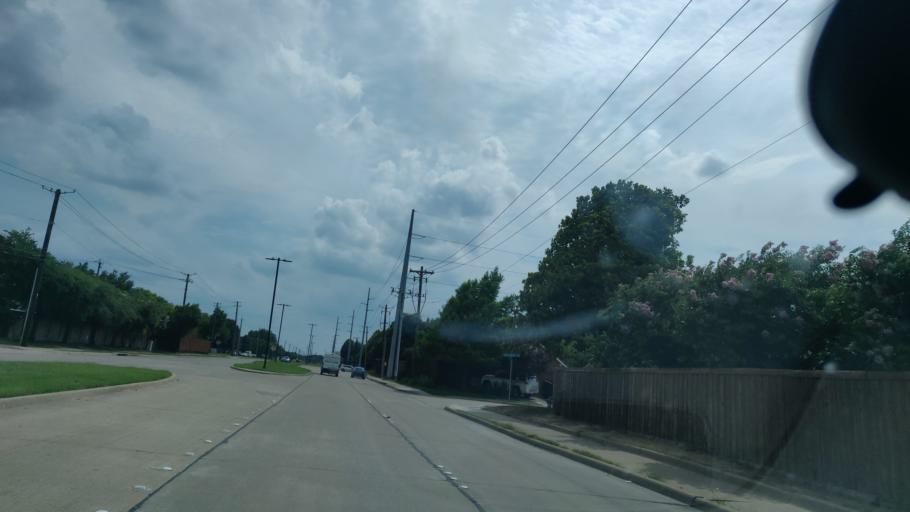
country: US
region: Texas
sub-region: Dallas County
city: Garland
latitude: 32.9349
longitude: -96.6084
